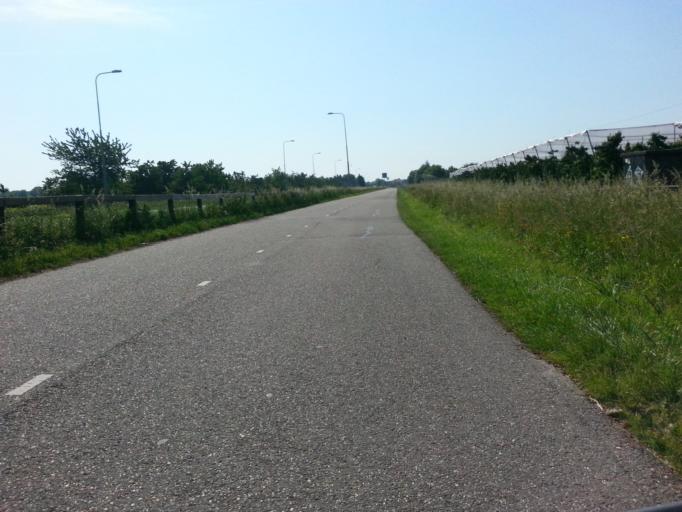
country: NL
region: Utrecht
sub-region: Gemeente Wijk bij Duurstede
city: Wijk bij Duurstede
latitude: 51.9898
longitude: 5.3281
